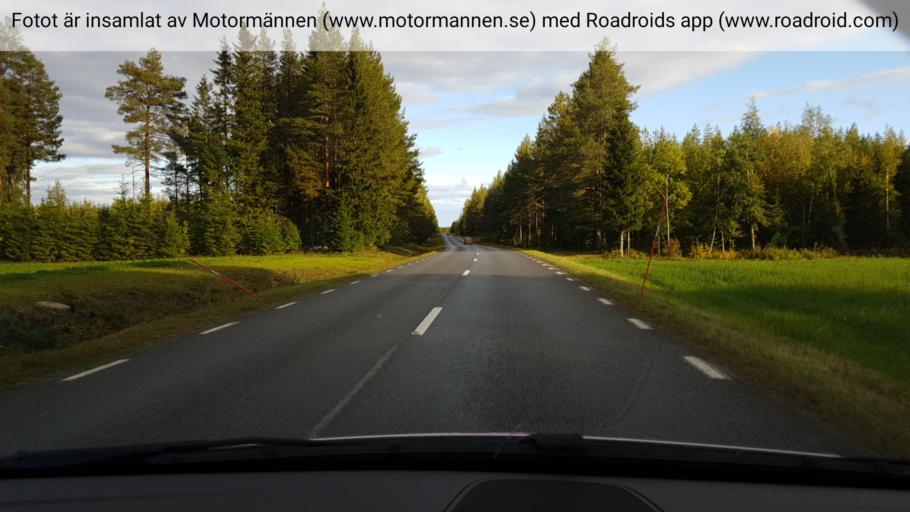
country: SE
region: Jaemtland
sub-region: Krokoms Kommun
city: Krokom
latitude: 63.1360
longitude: 14.1969
